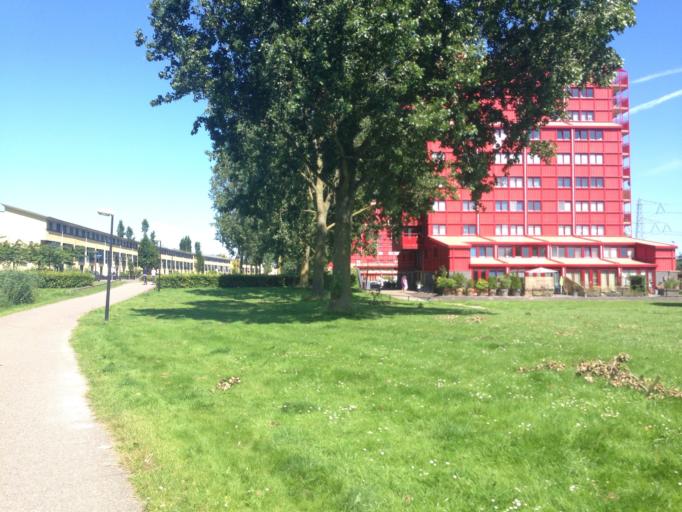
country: NL
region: Flevoland
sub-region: Gemeente Almere
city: Almere Stad
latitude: 52.3903
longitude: 5.2998
